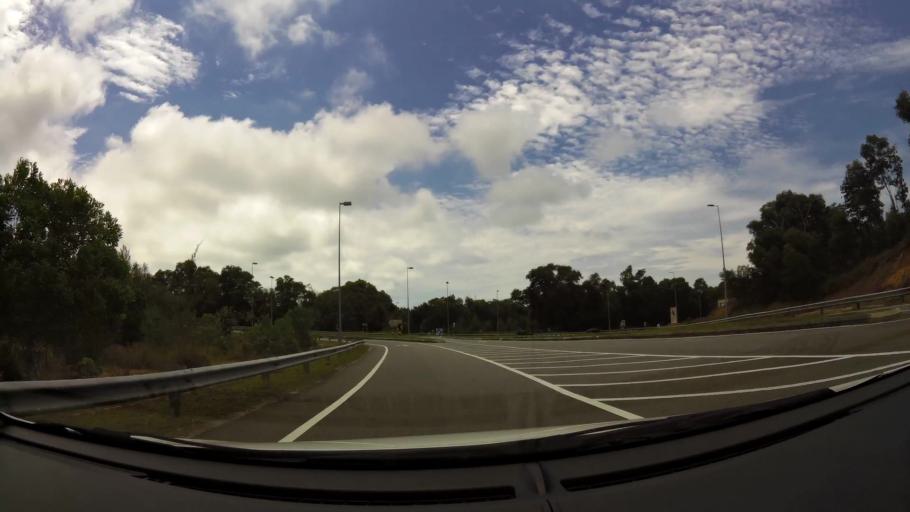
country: BN
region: Brunei and Muara
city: Bandar Seri Begawan
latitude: 4.9686
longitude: 114.8870
